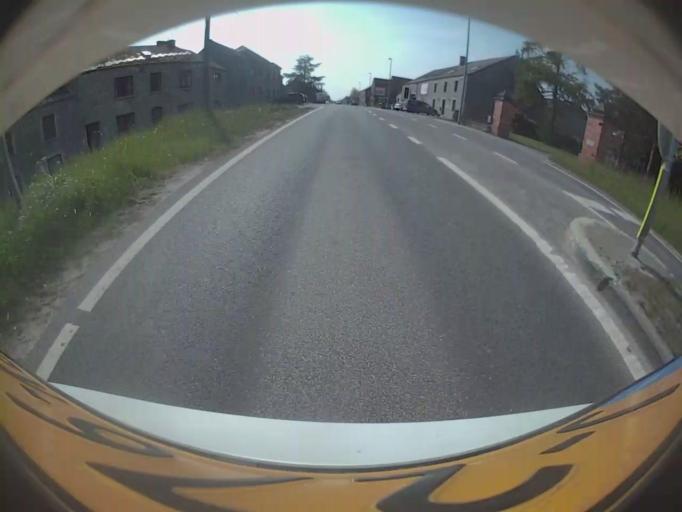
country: BE
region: Wallonia
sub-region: Province de Namur
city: Dinant
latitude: 50.2598
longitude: 4.9832
